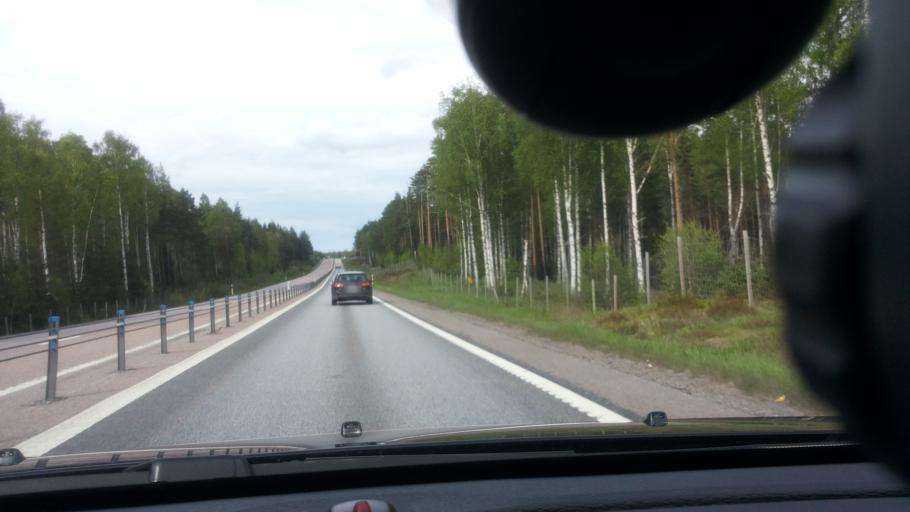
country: SE
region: Gaevleborg
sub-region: Soderhamns Kommun
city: Ljusne
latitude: 61.1005
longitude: 16.9917
